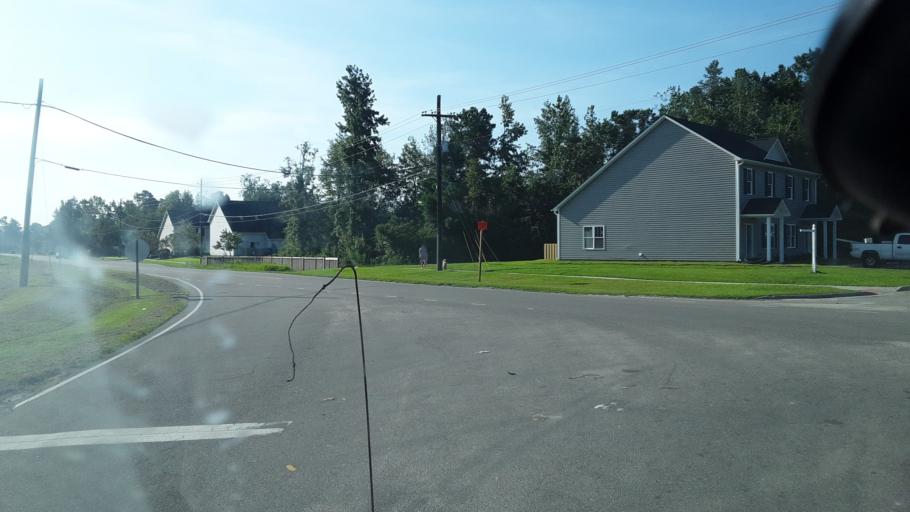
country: US
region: North Carolina
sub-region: Brunswick County
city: Leland
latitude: 34.2560
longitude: -78.0437
